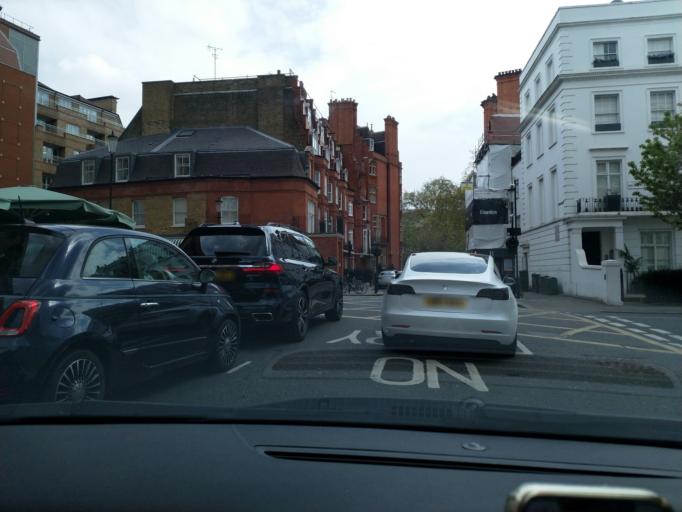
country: GB
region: England
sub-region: Greater London
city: Chelsea
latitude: 51.4985
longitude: -0.1625
